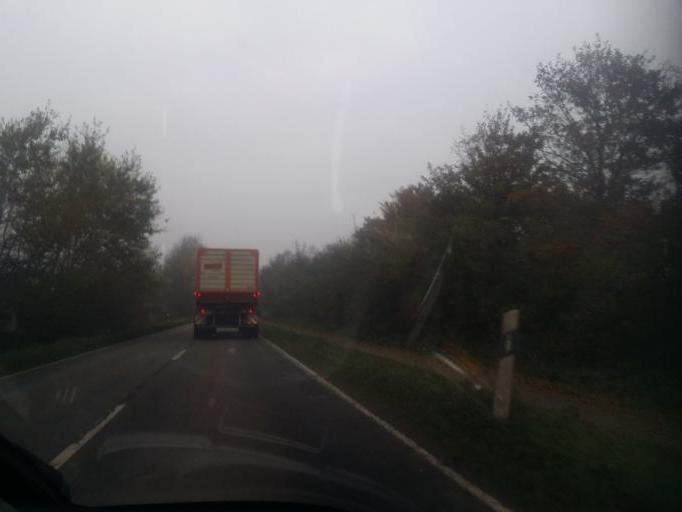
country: DE
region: Schleswig-Holstein
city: Grosssolt
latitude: 54.6842
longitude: 9.4923
